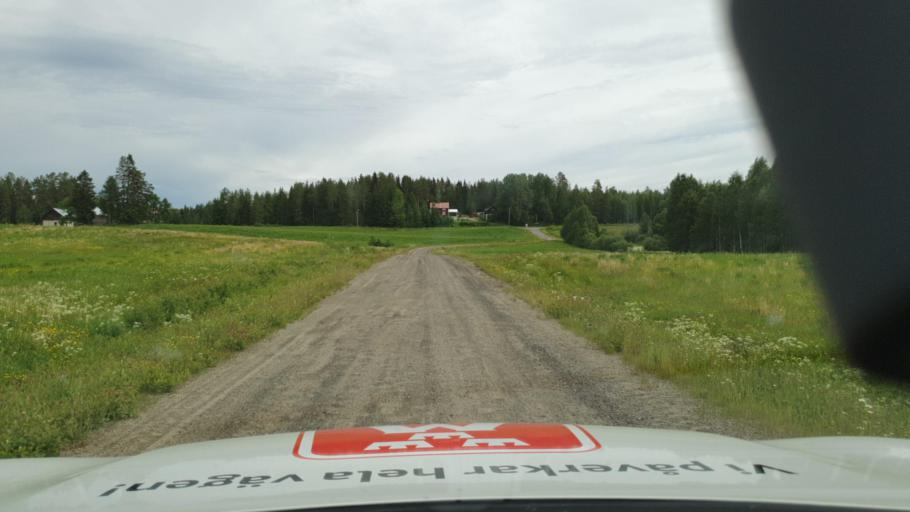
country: SE
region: Vaesterbotten
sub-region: Robertsfors Kommun
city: Robertsfors
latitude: 64.2715
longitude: 20.6902
